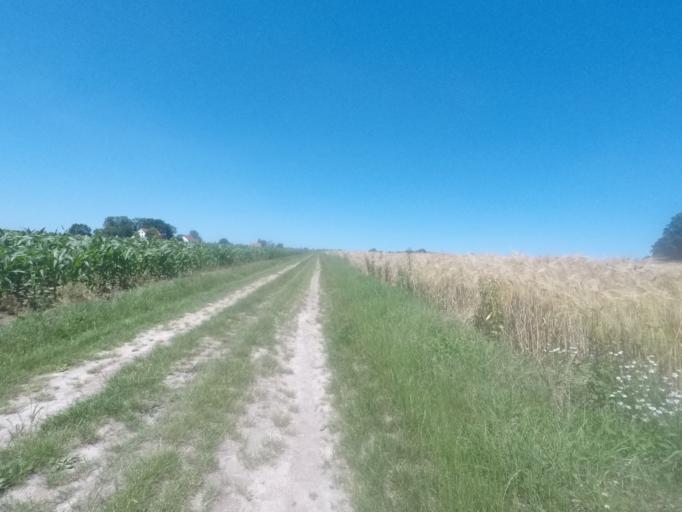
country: DE
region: North Rhine-Westphalia
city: Enger
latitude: 52.1328
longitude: 8.5938
